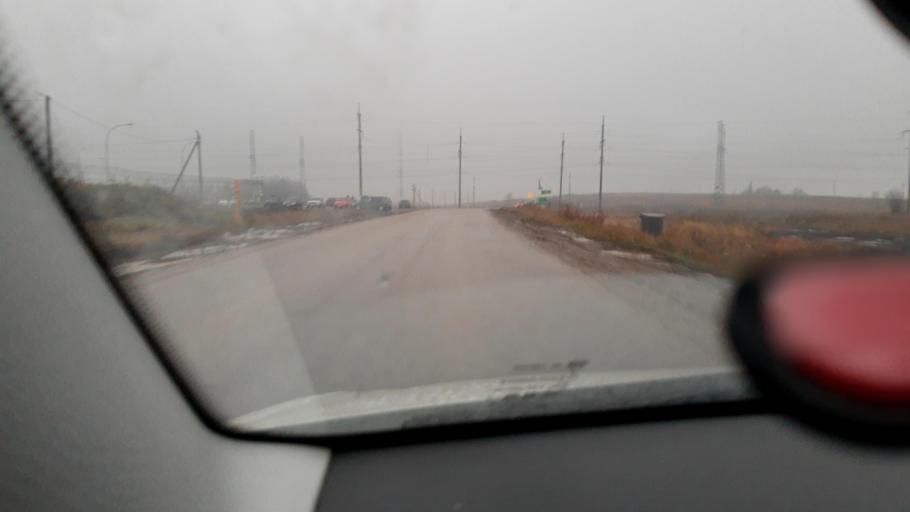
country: RU
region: Bashkortostan
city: Blagoveshchensk
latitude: 54.9021
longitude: 56.1697
